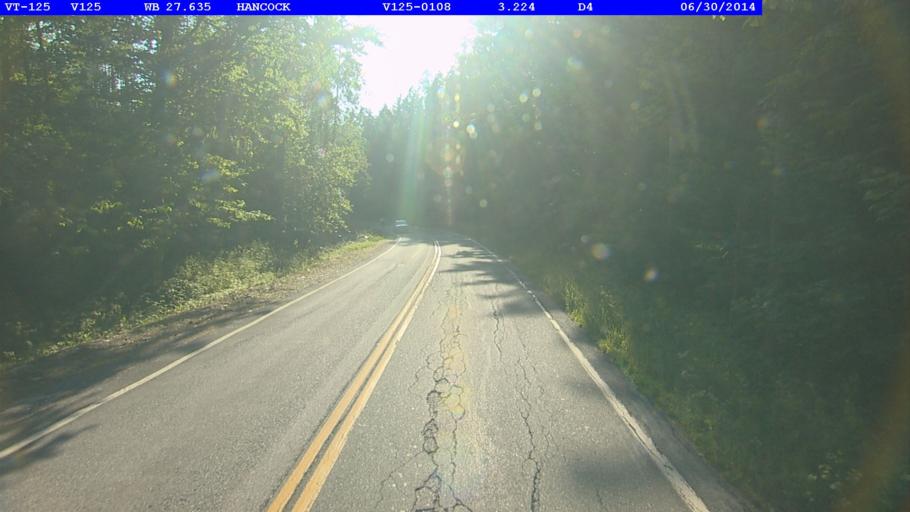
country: US
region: Vermont
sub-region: Rutland County
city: Brandon
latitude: 43.9275
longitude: -72.9183
